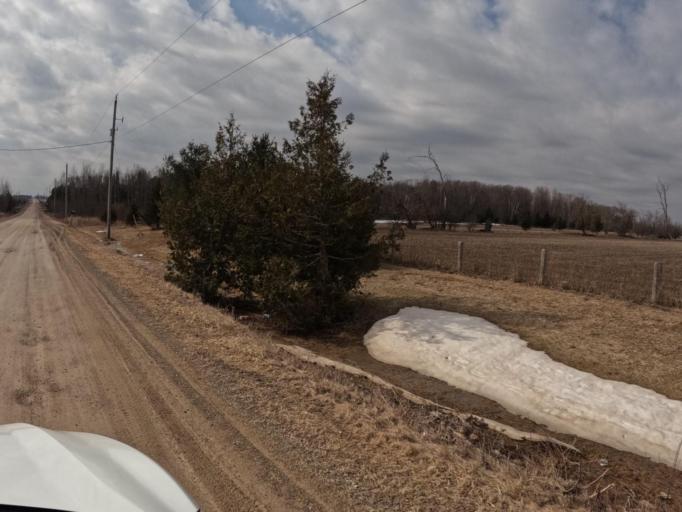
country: CA
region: Ontario
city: Orangeville
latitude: 43.9321
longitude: -80.2208
